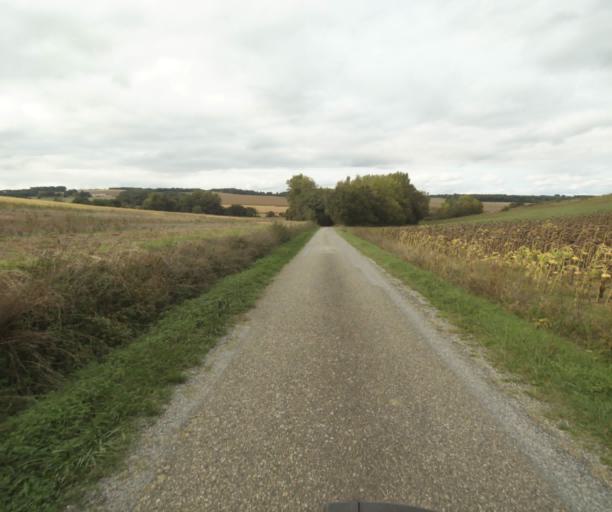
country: FR
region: Midi-Pyrenees
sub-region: Departement du Tarn-et-Garonne
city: Beaumont-de-Lomagne
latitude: 43.8291
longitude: 1.0700
